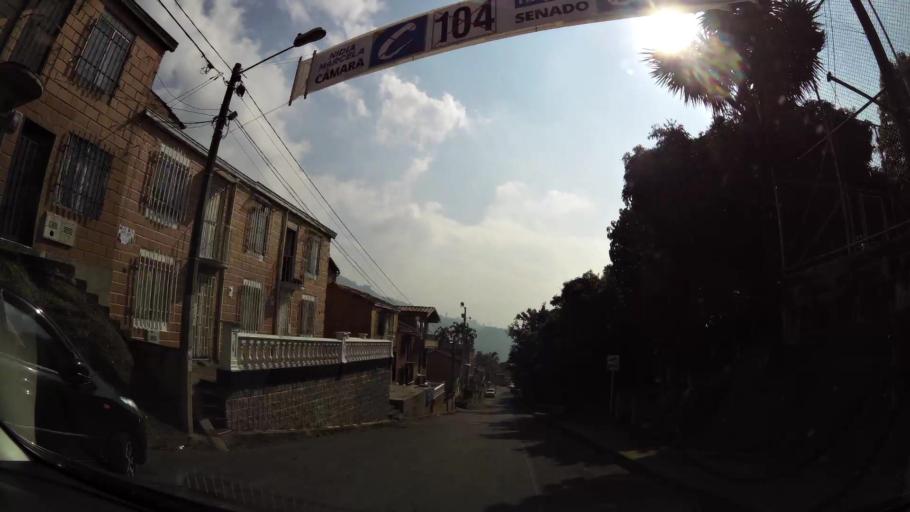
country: CO
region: Antioquia
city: La Estrella
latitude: 6.1711
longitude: -75.6383
